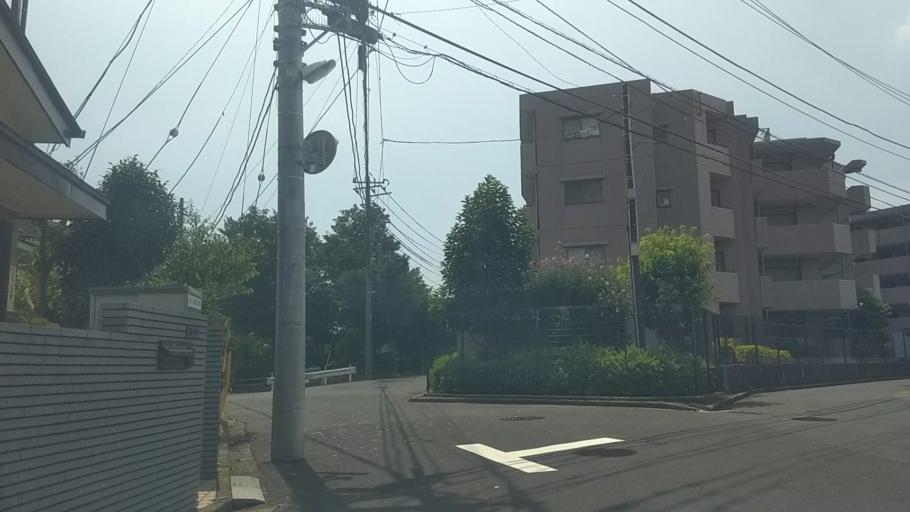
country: JP
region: Kanagawa
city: Yokohama
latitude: 35.4966
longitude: 139.6578
